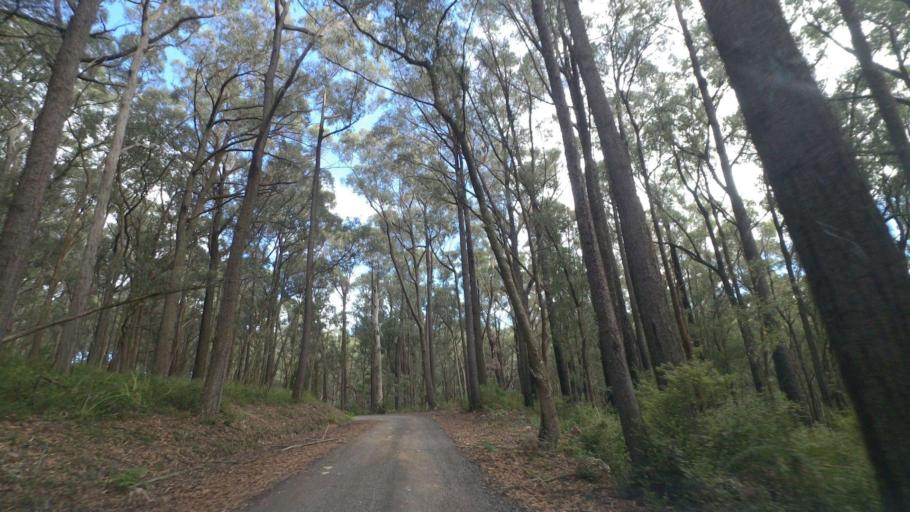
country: AU
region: Victoria
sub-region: Cardinia
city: Gembrook
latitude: -37.9168
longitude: 145.6341
